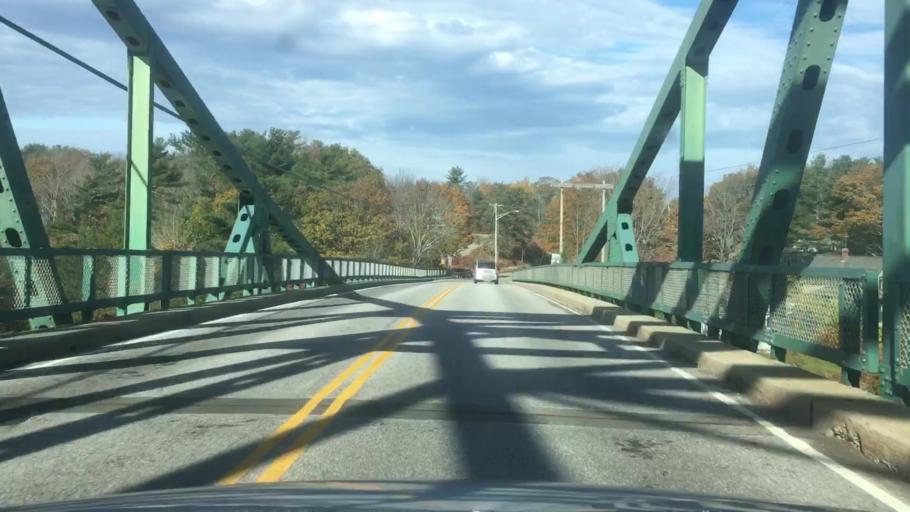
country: US
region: Maine
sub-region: Sagadahoc County
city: Woolwich
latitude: 43.9094
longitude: -69.8004
